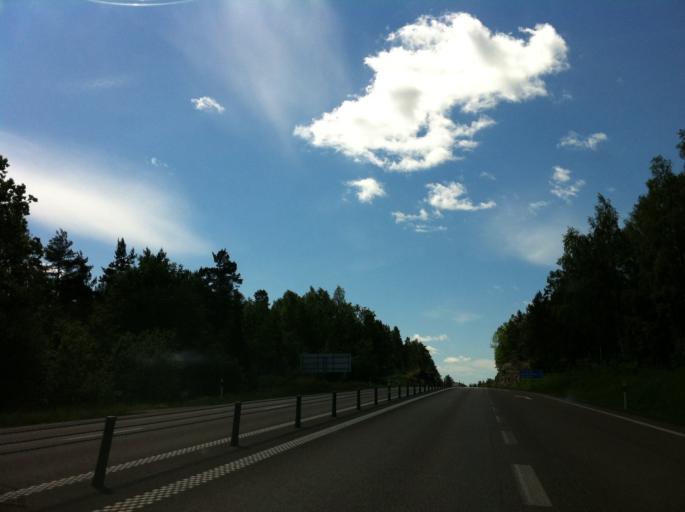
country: SE
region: Vaestra Goetaland
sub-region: Melleruds Kommun
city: Mellerud
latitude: 58.7739
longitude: 12.4968
